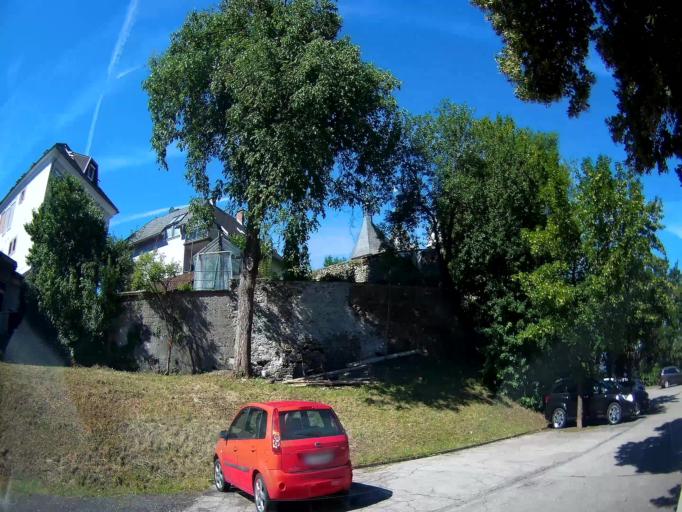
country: AT
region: Carinthia
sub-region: Politischer Bezirk Klagenfurt Land
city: Maria Saal
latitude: 46.6817
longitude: 14.3476
